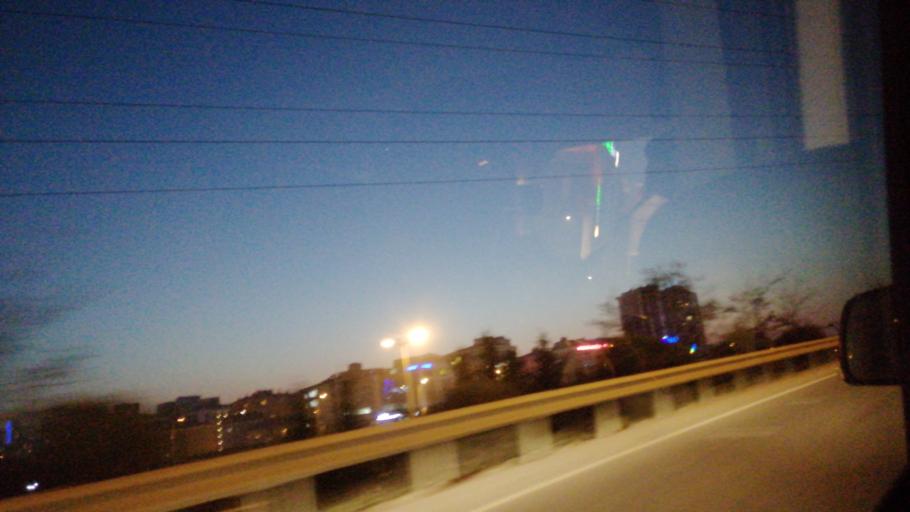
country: TR
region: Istanbul
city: Umraniye
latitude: 40.9959
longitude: 29.1456
